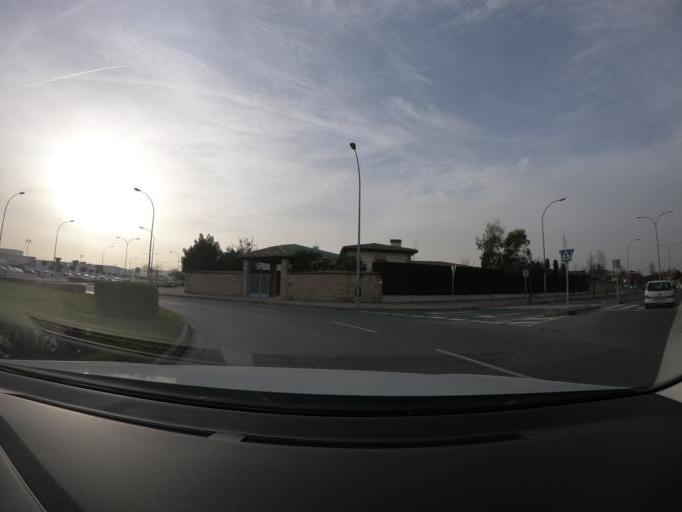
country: ES
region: La Rioja
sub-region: Provincia de La Rioja
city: Logrono
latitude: 42.4537
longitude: -2.4711
